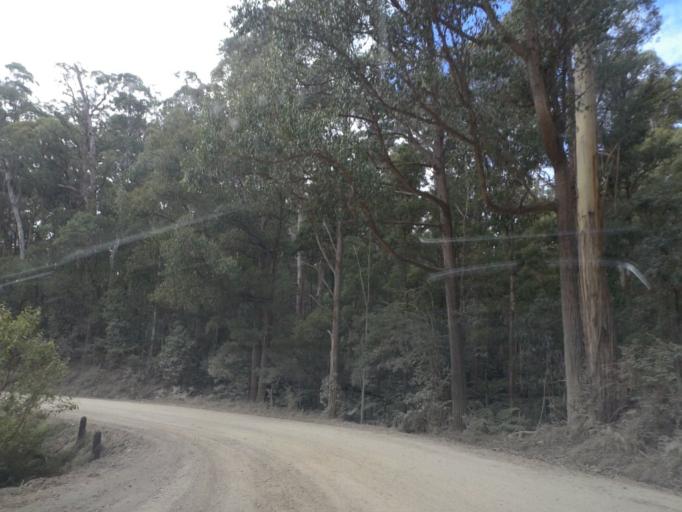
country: AU
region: Victoria
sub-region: Yarra Ranges
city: Millgrove
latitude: -37.5106
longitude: 145.9613
